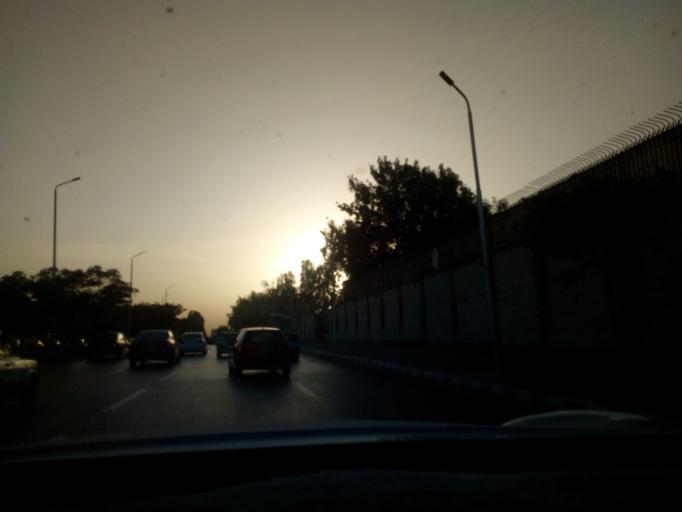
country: EG
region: Muhafazat al Qalyubiyah
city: Al Khankah
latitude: 30.1052
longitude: 31.3595
